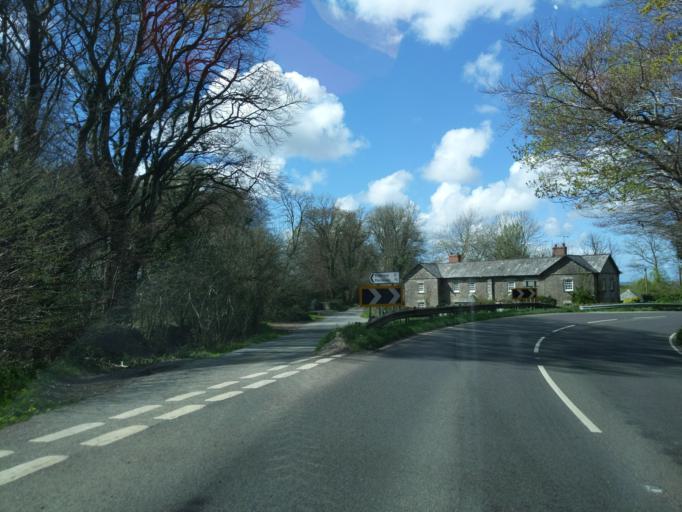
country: GB
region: England
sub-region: Cornwall
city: Bodmin
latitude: 50.4978
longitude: -4.7749
